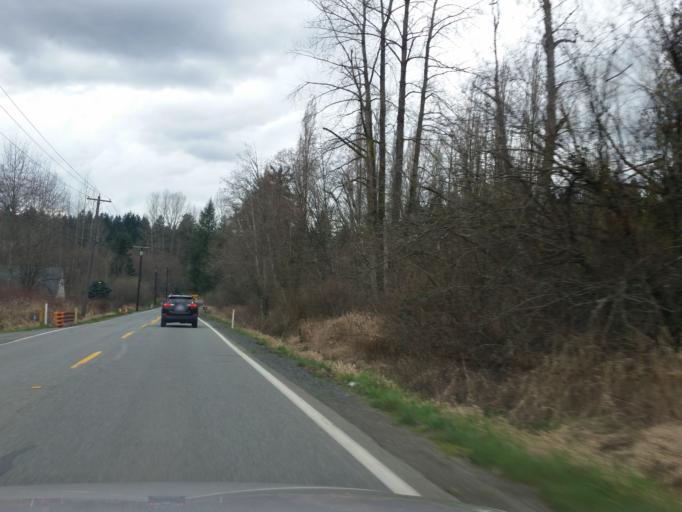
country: US
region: Washington
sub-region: Snohomish County
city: North Creek
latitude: 47.8051
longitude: -122.1559
